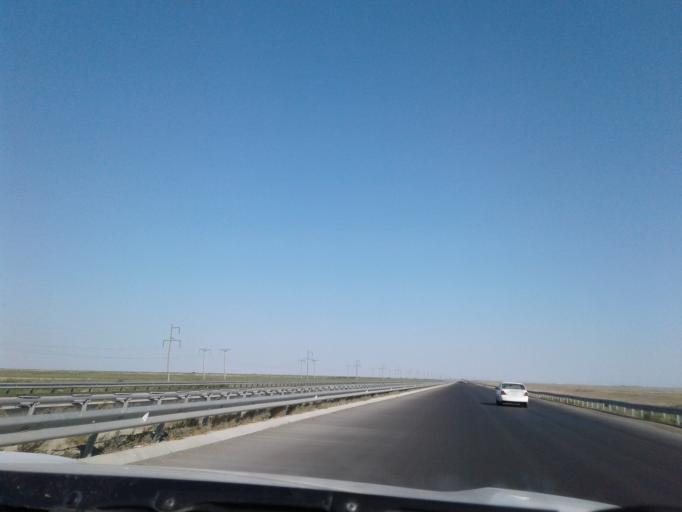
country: TM
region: Balkan
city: Gazanjyk
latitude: 39.2390
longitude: 55.6817
